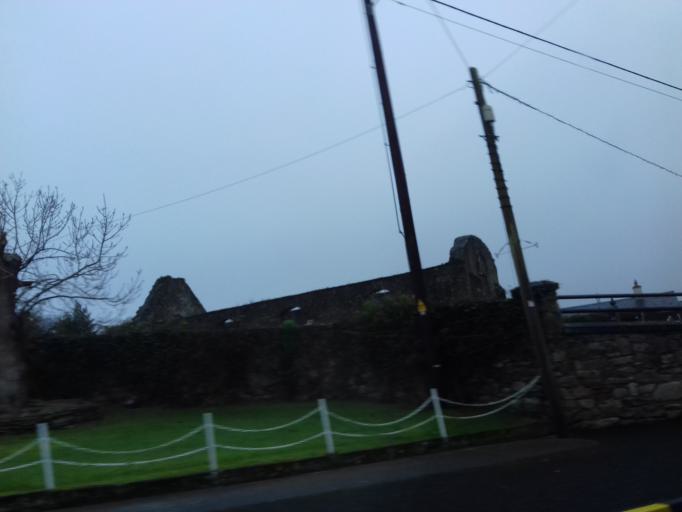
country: IE
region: Ulster
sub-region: County Donegal
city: Ramelton
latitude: 55.0357
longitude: -7.6453
